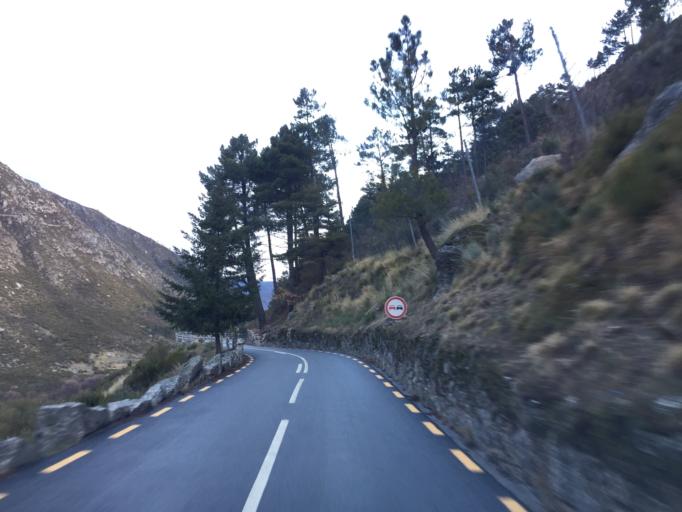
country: PT
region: Guarda
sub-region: Manteigas
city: Manteigas
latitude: 40.3496
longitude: -7.5603
